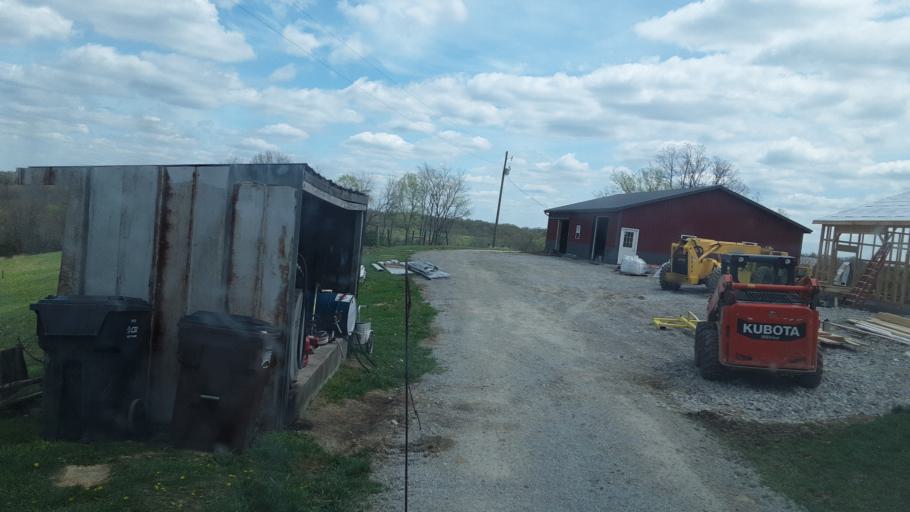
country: US
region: Kentucky
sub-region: Owen County
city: Owenton
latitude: 38.6765
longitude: -84.7811
